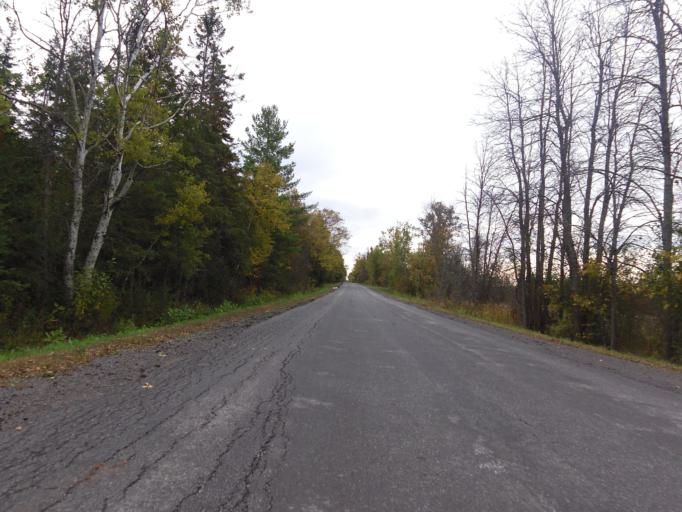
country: CA
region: Ontario
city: Arnprior
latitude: 45.4533
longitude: -76.1351
